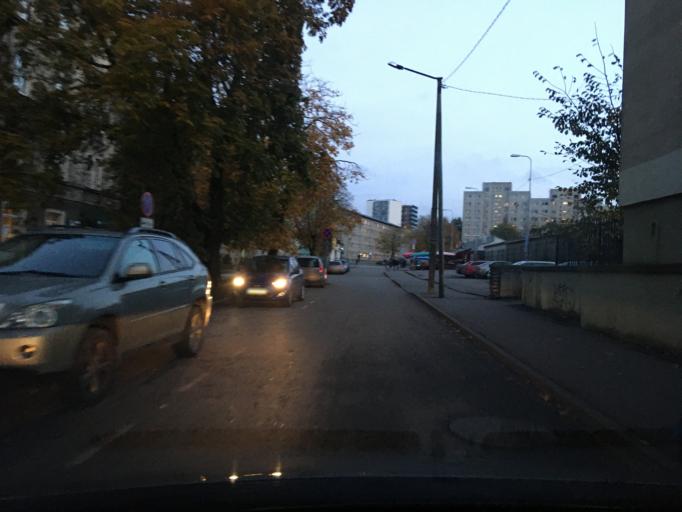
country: EE
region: Harju
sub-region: Tallinna linn
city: Tallinn
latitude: 59.4312
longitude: 24.7656
